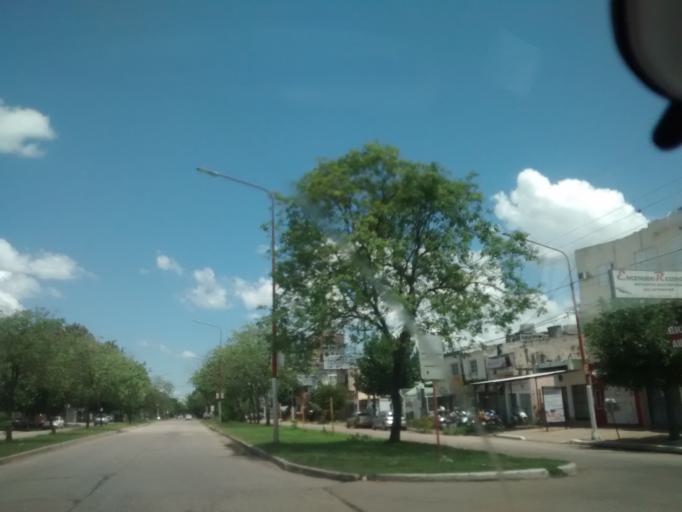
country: AR
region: Chaco
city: Resistencia
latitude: -27.4559
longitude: -58.9953
